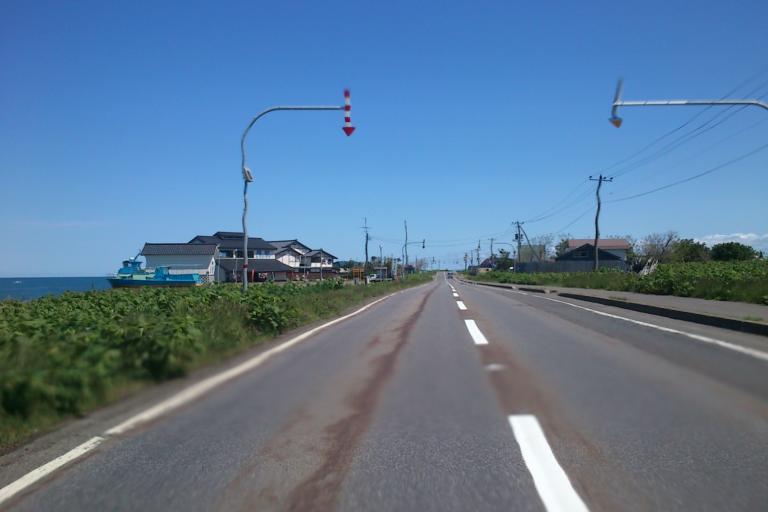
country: JP
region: Hokkaido
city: Rumoi
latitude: 43.8471
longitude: 141.5043
